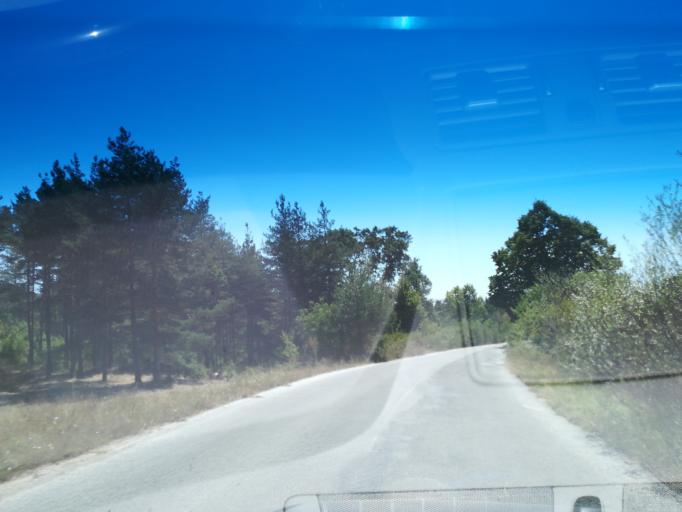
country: BG
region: Pazardzhik
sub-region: Obshtina Strelcha
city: Strelcha
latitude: 42.5378
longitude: 24.3344
